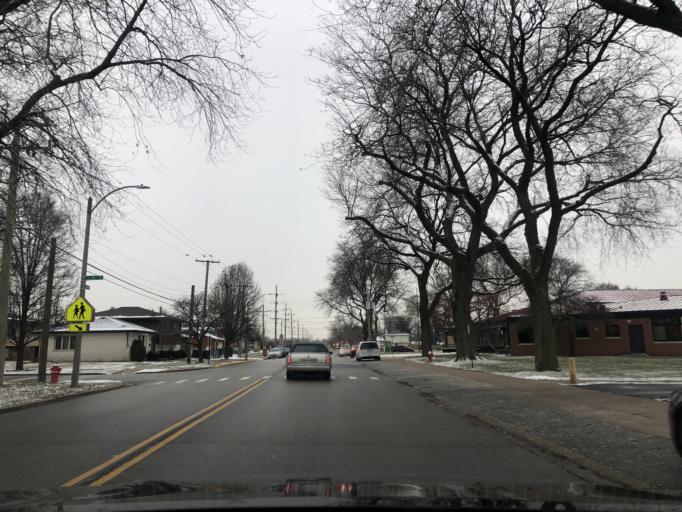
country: US
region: Illinois
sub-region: Cook County
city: Evergreen Park
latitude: 41.7294
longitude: -87.6922
